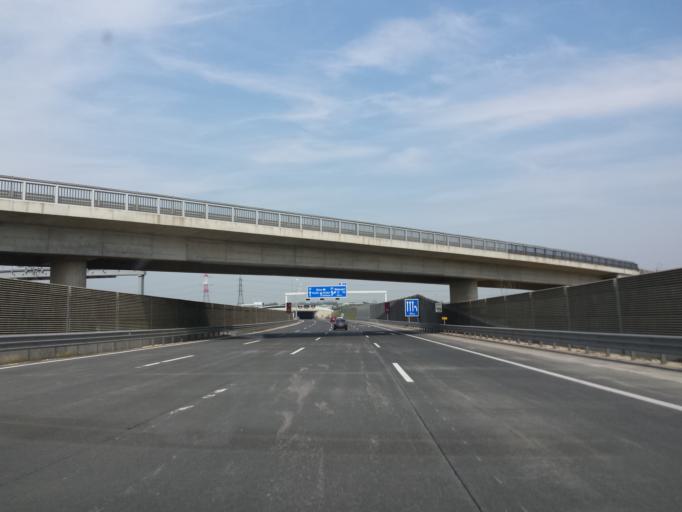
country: AT
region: Lower Austria
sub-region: Politischer Bezirk Mistelbach
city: Grossebersdorf
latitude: 48.3540
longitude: 16.4832
